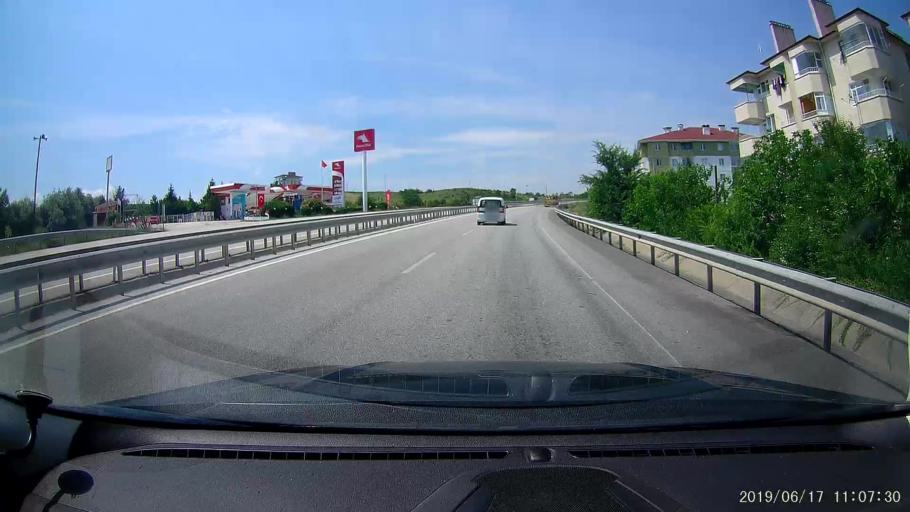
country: TR
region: Kastamonu
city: Tosya
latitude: 41.0016
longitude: 34.0541
